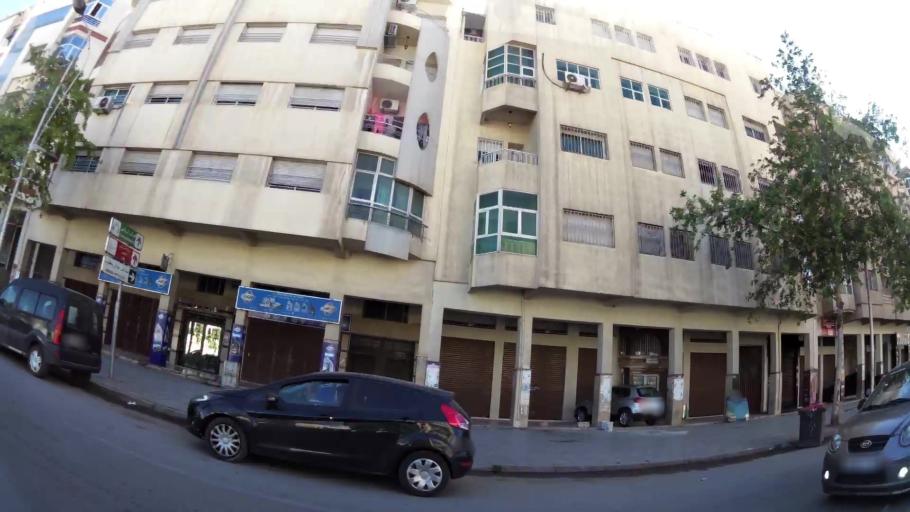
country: MA
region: Fes-Boulemane
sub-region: Fes
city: Fes
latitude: 34.0200
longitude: -4.9872
